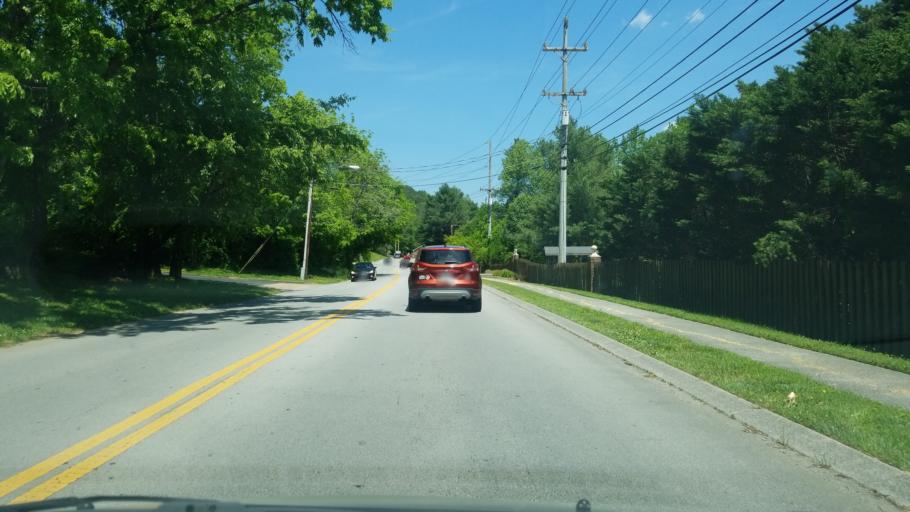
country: US
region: Tennessee
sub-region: Hamilton County
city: Signal Mountain
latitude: 35.1051
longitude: -85.3269
